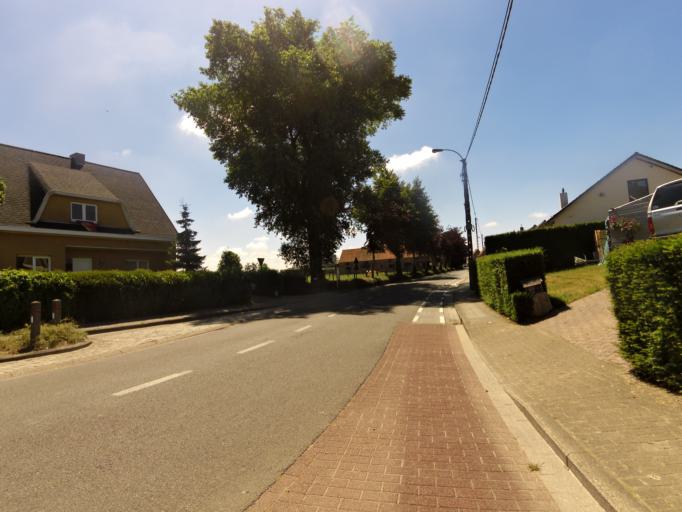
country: BE
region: Flanders
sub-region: Provincie West-Vlaanderen
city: Ichtegem
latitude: 51.1299
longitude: 3.0341
